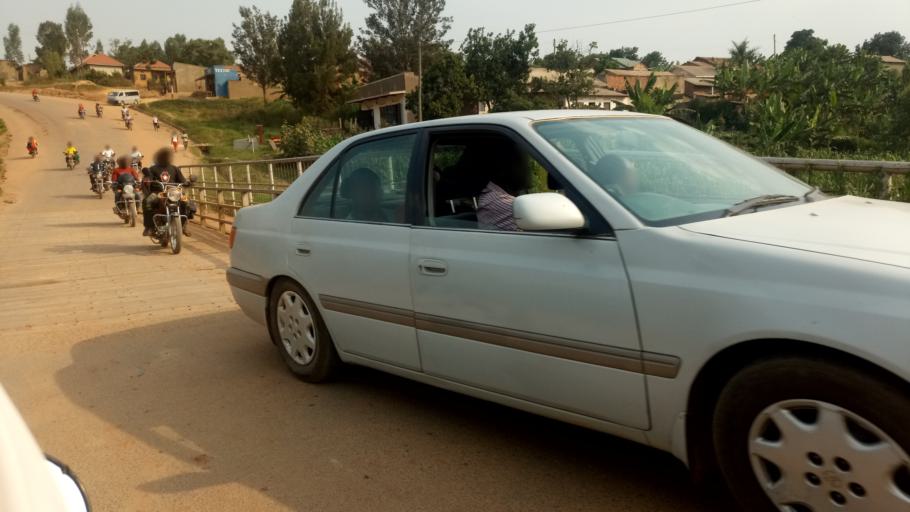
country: UG
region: Western Region
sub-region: Mbarara District
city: Mbarara
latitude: -0.6166
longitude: 30.6683
